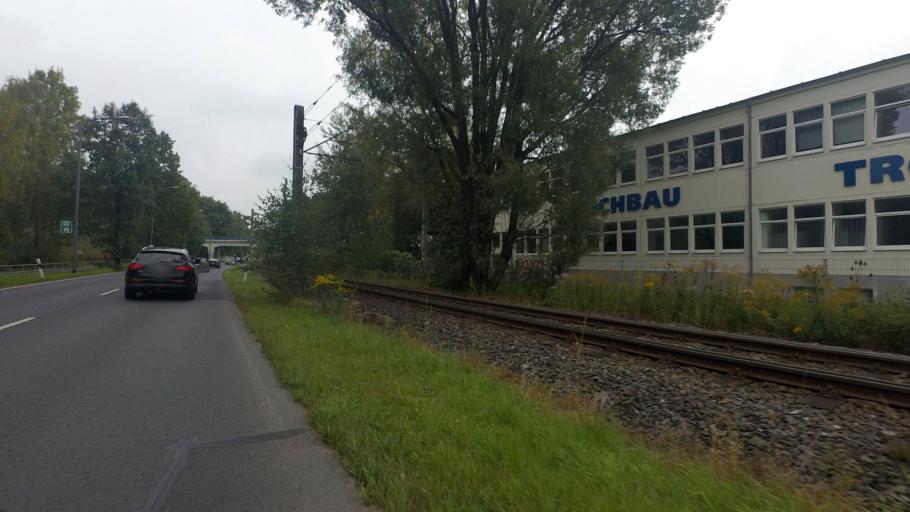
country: DE
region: Saxony
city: Albertstadt
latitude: 51.1261
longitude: 13.7920
